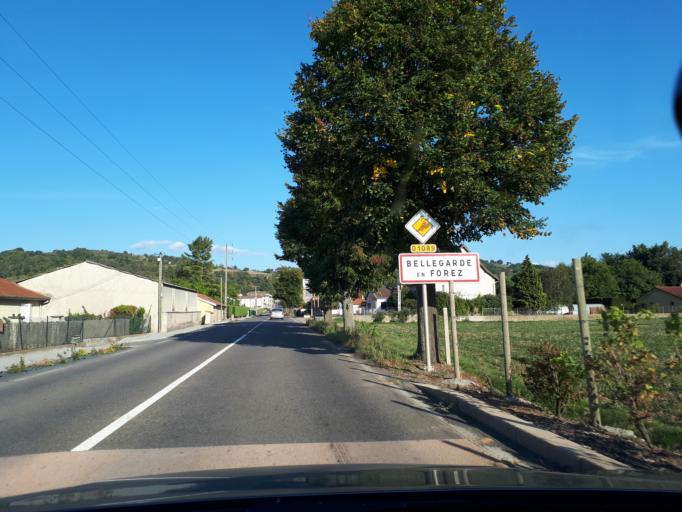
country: FR
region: Rhone-Alpes
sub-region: Departement de la Loire
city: Bellegarde-en-Forez
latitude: 45.6464
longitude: 4.2887
